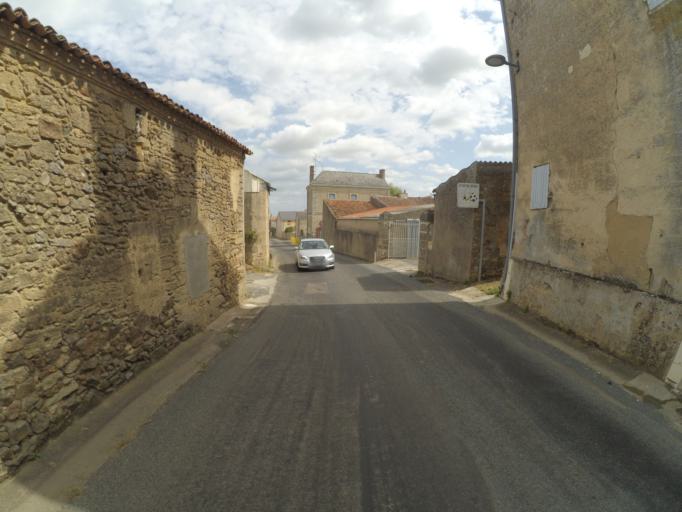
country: FR
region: Pays de la Loire
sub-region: Departement de Maine-et-Loire
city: Saint-Jean
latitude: 47.1953
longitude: -0.3676
